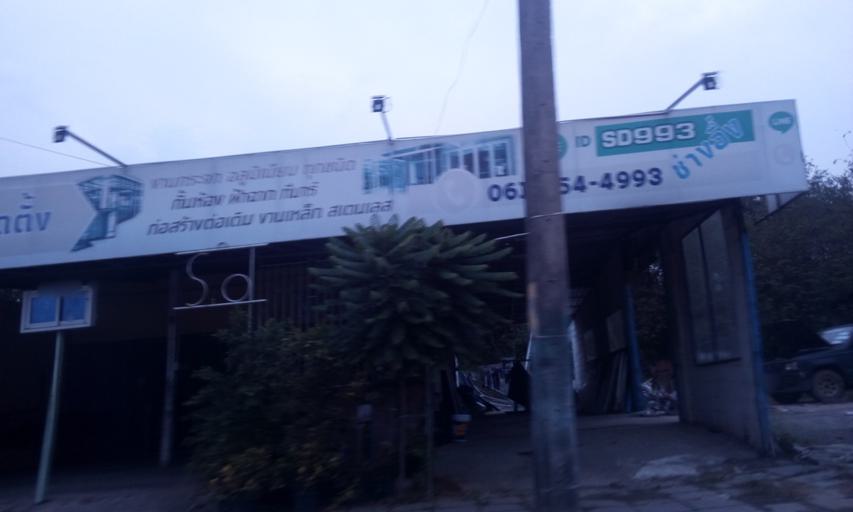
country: TH
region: Chon Buri
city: Ko Chan
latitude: 13.4863
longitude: 101.2777
